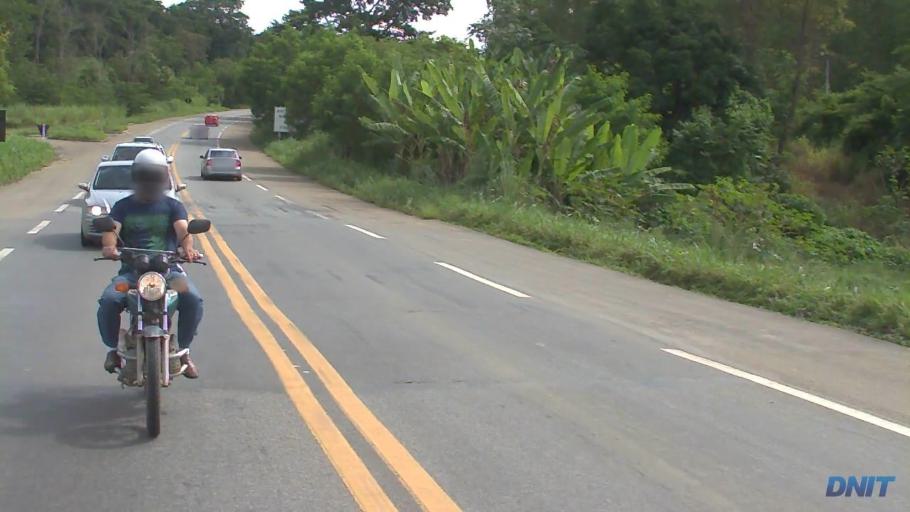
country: BR
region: Minas Gerais
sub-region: Ipaba
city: Ipaba
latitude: -19.3449
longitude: -42.4322
